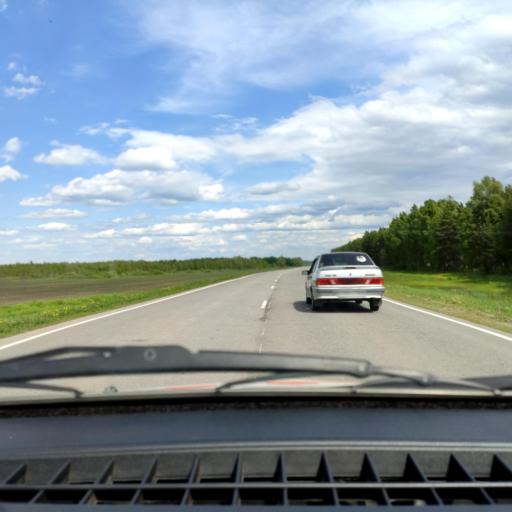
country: RU
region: Bashkortostan
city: Krasnaya Gorka
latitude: 55.0540
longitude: 56.5357
